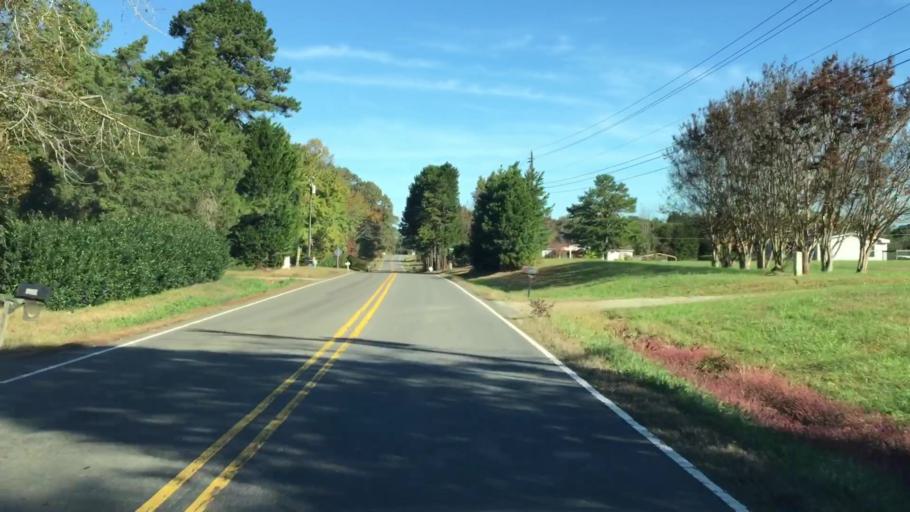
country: US
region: North Carolina
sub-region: Iredell County
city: Mooresville
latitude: 35.6039
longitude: -80.7554
